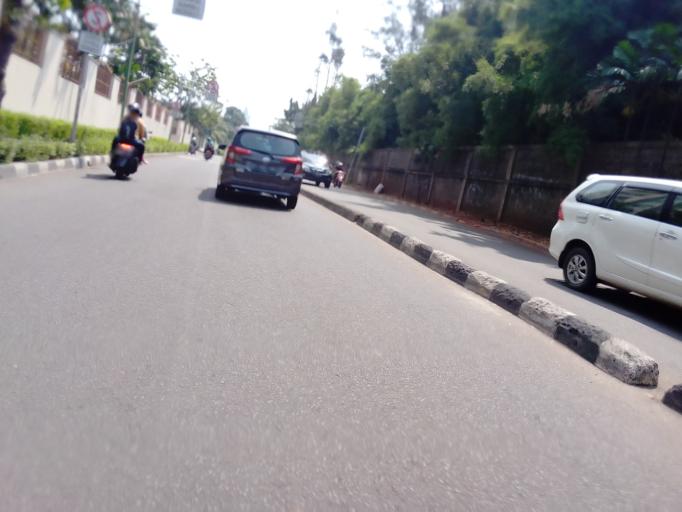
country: ID
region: Jakarta Raya
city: Jakarta
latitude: -6.2230
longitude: 106.7948
